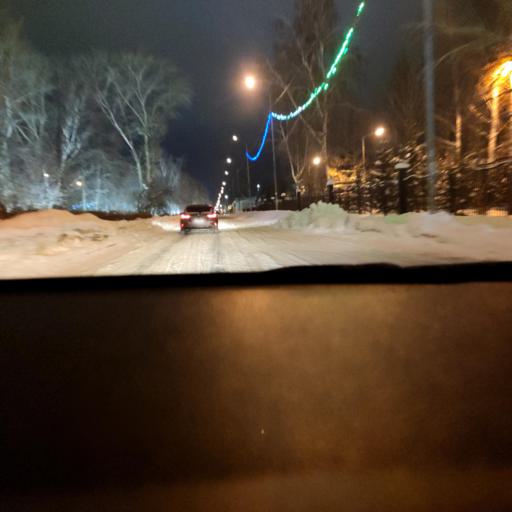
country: RU
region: Tatarstan
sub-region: Chistopol'skiy Rayon
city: Chistopol'
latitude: 55.3645
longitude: 50.6449
